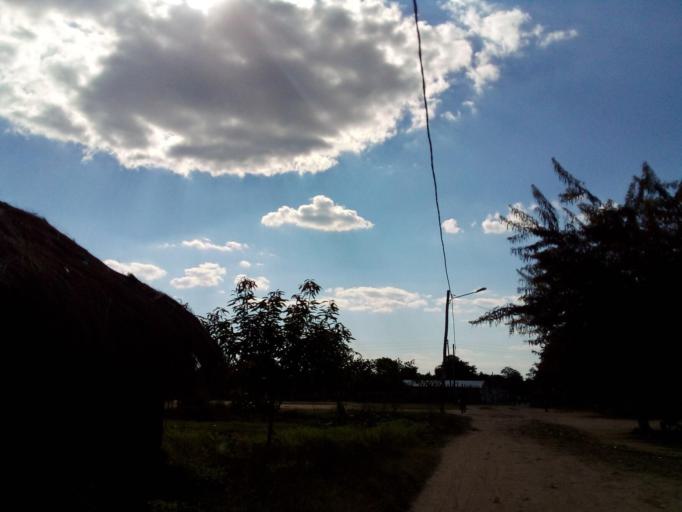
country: MZ
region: Zambezia
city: Quelimane
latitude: -17.5700
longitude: 36.7007
